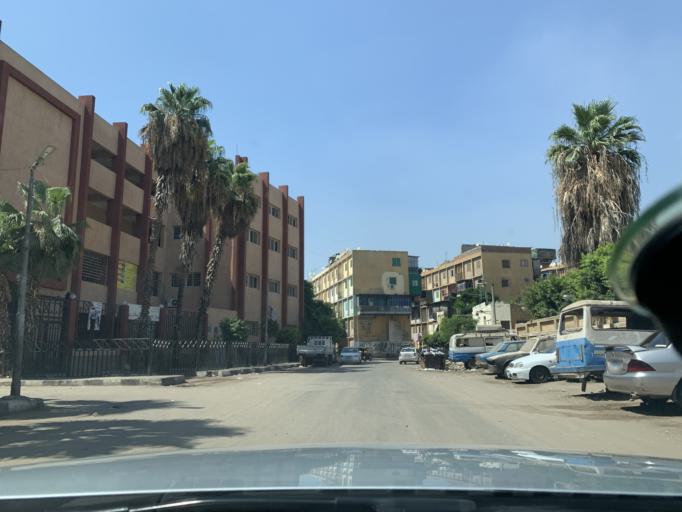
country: EG
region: Muhafazat al Qahirah
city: Cairo
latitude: 30.0751
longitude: 31.2574
